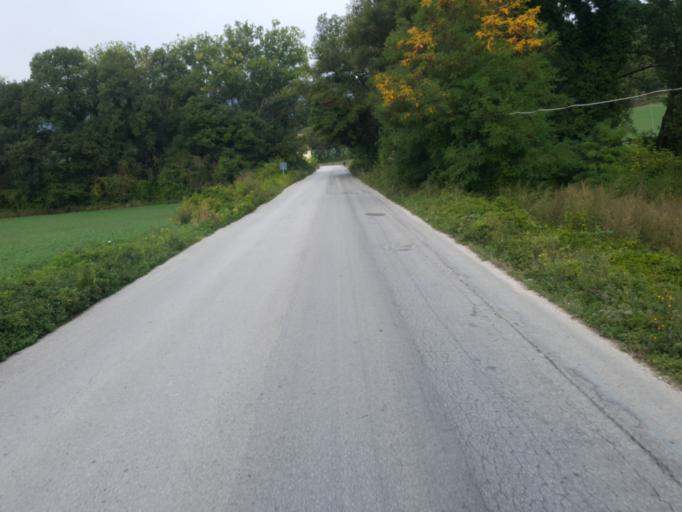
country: IT
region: The Marches
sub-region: Provincia di Ancona
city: Fabriano
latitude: 43.3458
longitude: 12.8587
